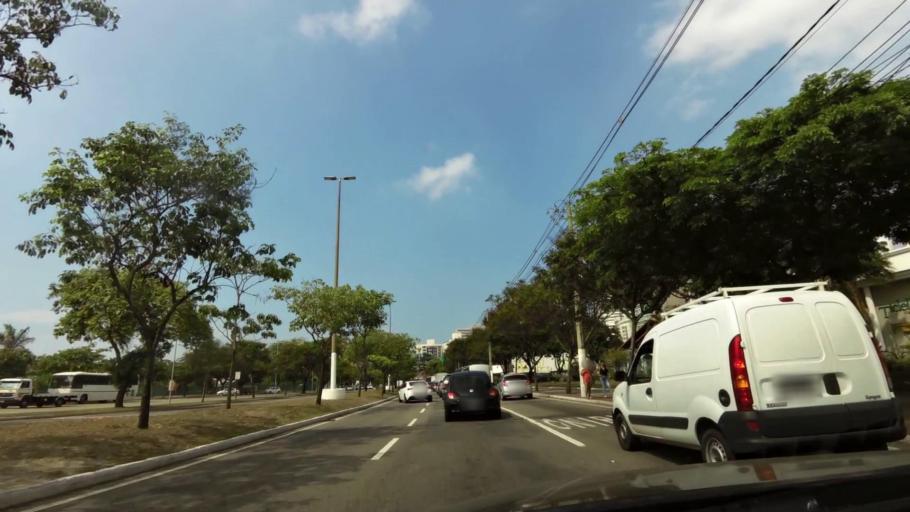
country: BR
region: Espirito Santo
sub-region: Vila Velha
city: Vila Velha
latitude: -20.3067
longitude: -40.2920
